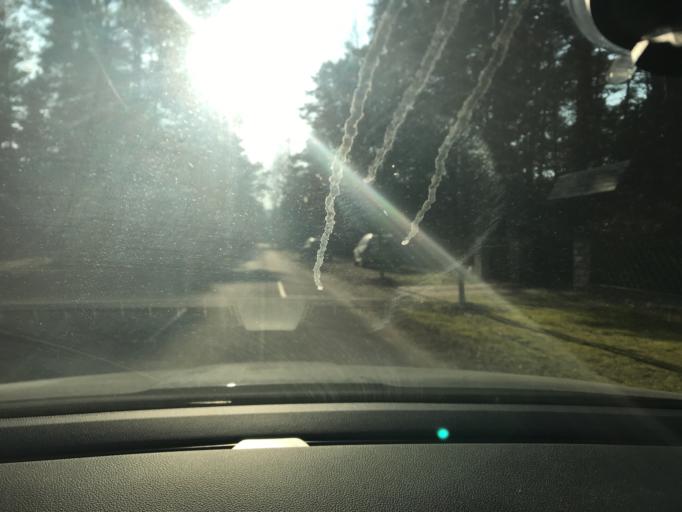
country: DE
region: Brandenburg
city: Munchehofe
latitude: 52.2151
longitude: 13.7946
